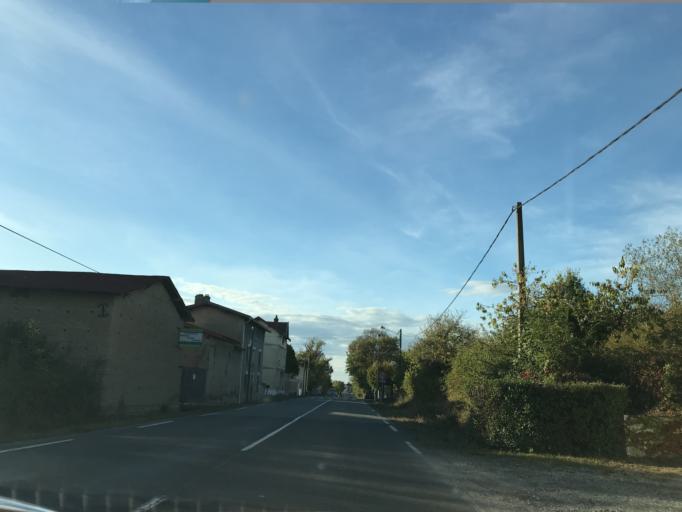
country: FR
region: Auvergne
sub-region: Departement du Puy-de-Dome
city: Paslieres
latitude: 45.9242
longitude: 3.5046
